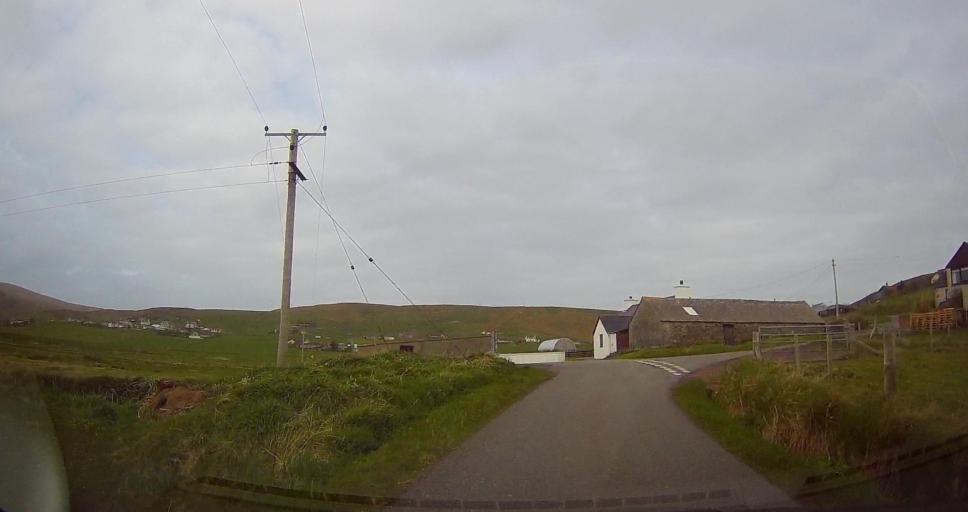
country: GB
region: Scotland
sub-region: Shetland Islands
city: Sandwick
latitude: 60.0474
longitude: -1.2144
